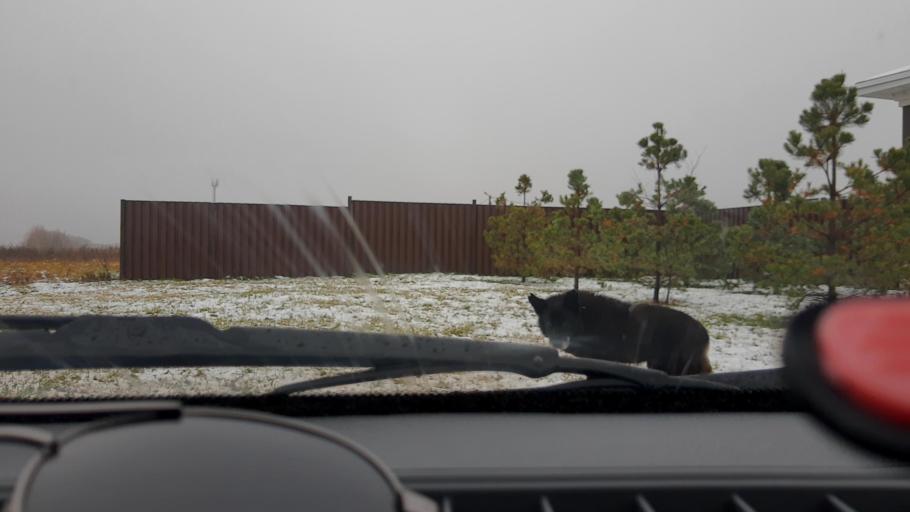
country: RU
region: Bashkortostan
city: Kabakovo
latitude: 54.5950
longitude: 56.2196
